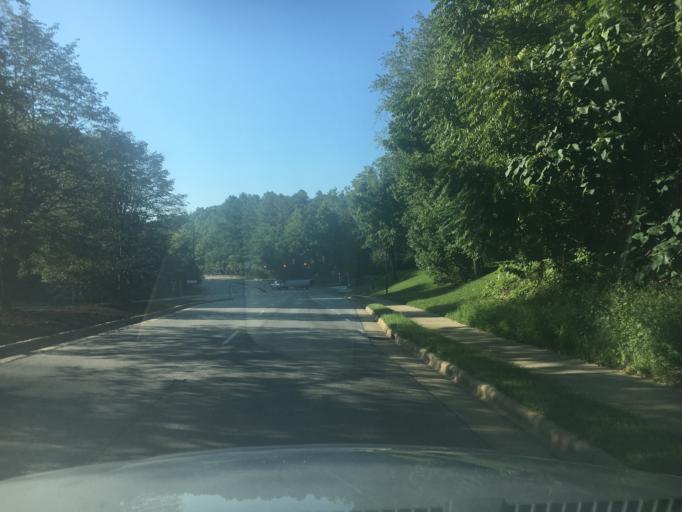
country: US
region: North Carolina
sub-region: Buncombe County
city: Asheville
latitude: 35.6103
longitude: -82.5656
